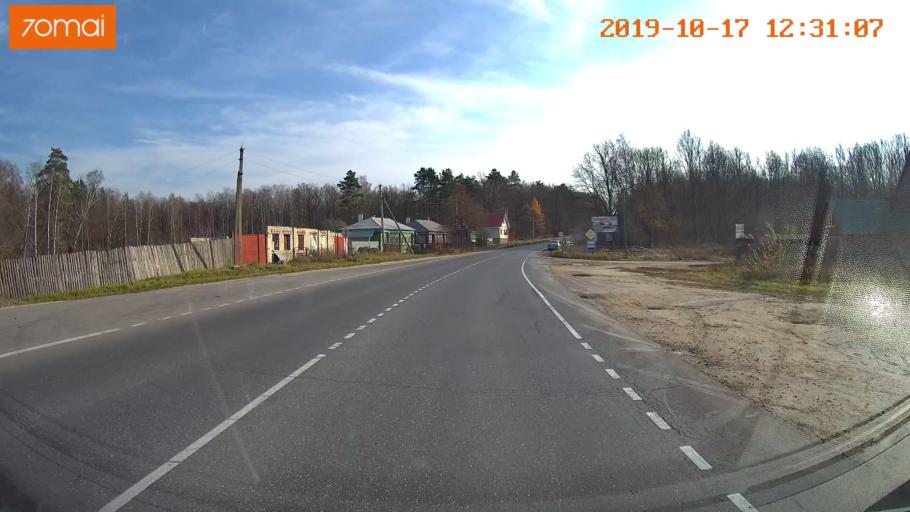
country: RU
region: Rjazan
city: Syntul
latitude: 54.9710
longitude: 41.3298
